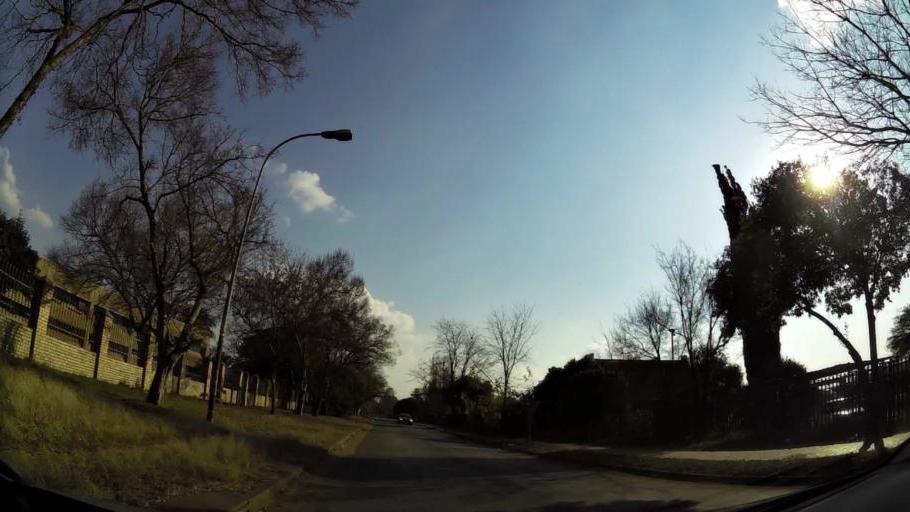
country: ZA
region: Gauteng
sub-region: Ekurhuleni Metropolitan Municipality
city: Tembisa
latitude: -25.9528
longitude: 28.2315
